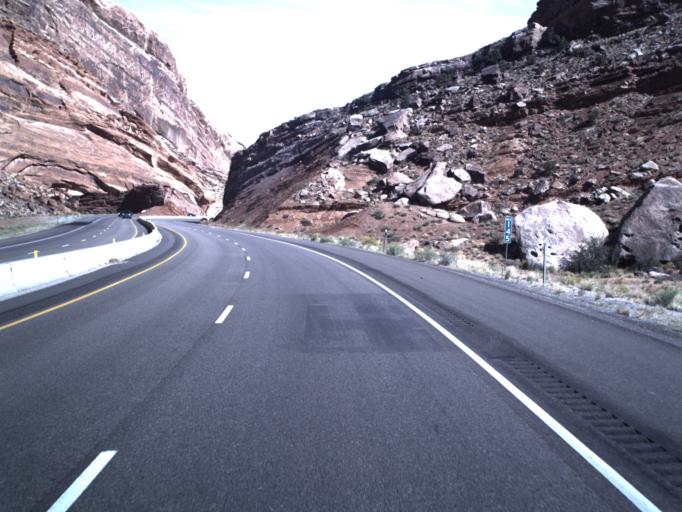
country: US
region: Utah
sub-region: Carbon County
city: East Carbon City
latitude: 38.9243
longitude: -110.4511
